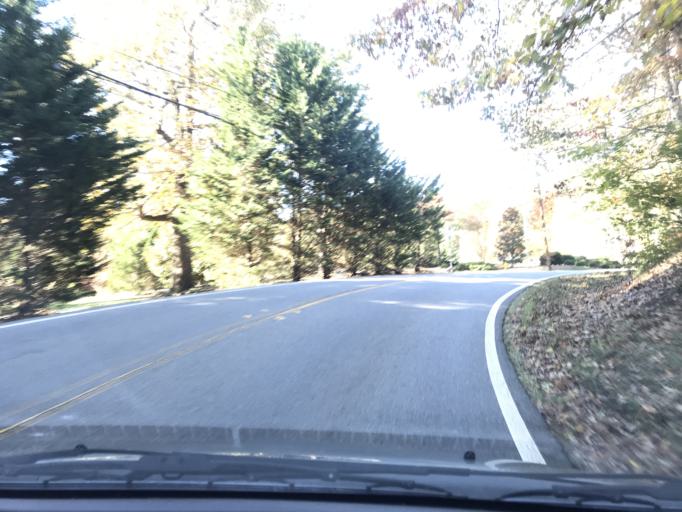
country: US
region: Georgia
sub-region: Walker County
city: Lookout Mountain
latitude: 34.9756
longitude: -85.3632
